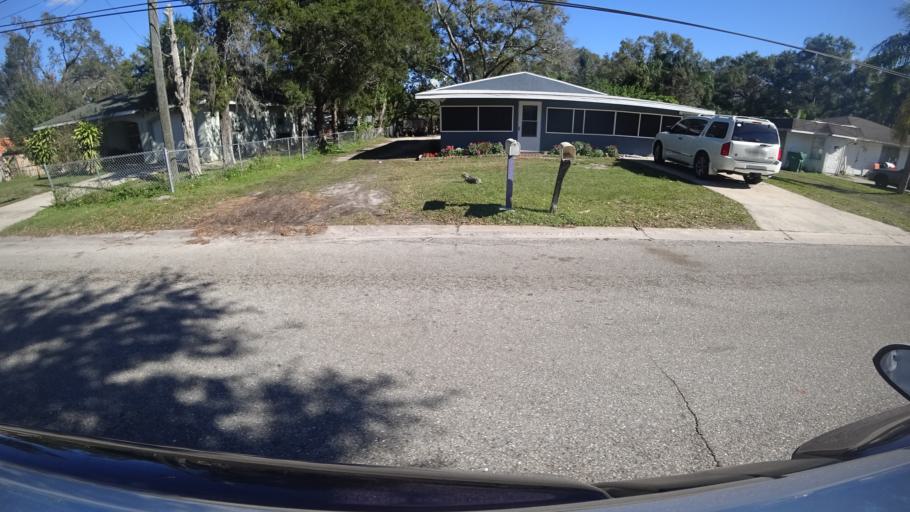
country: US
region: Florida
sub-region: Manatee County
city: West Samoset
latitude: 27.4393
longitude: -82.5523
